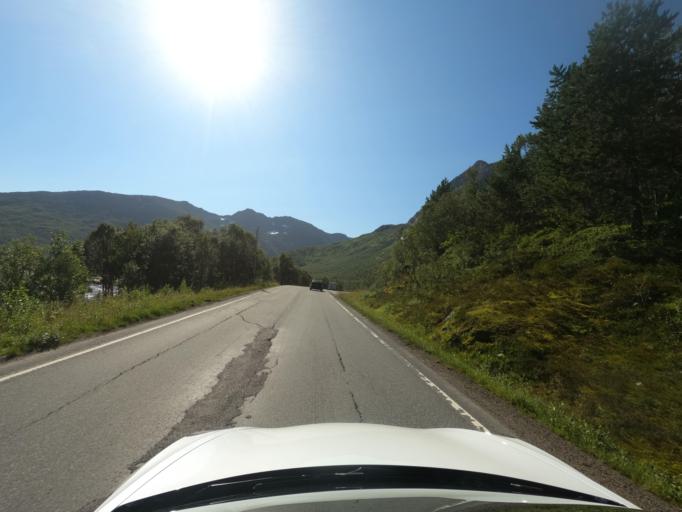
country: NO
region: Nordland
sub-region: Lodingen
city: Lodingen
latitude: 68.5359
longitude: 15.7227
